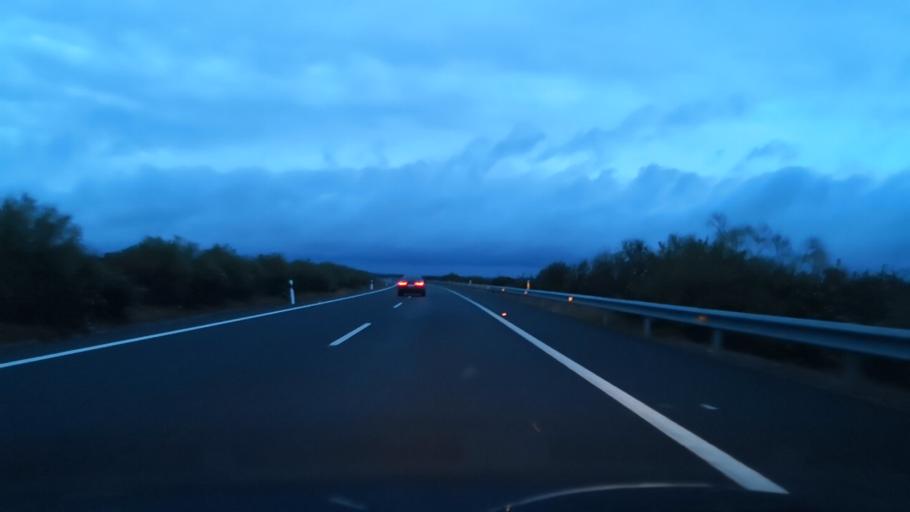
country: ES
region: Extremadura
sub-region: Provincia de Caceres
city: Casas de Don Antonio
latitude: 39.2134
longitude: -6.2874
